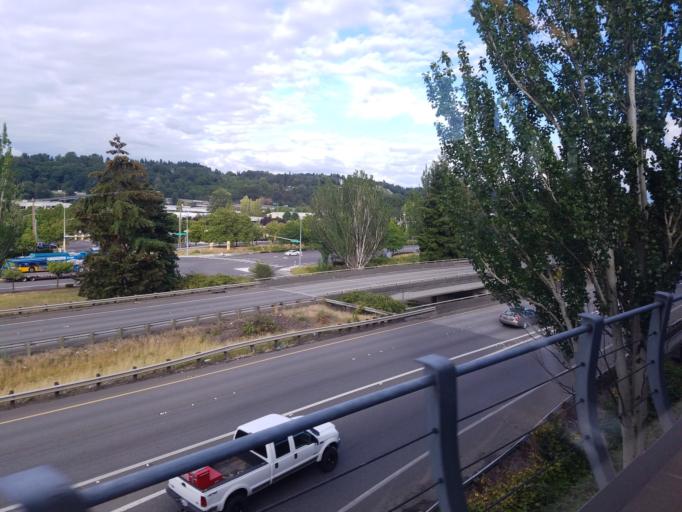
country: US
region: Washington
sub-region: King County
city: Riverton
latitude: 47.4857
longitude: -122.2764
